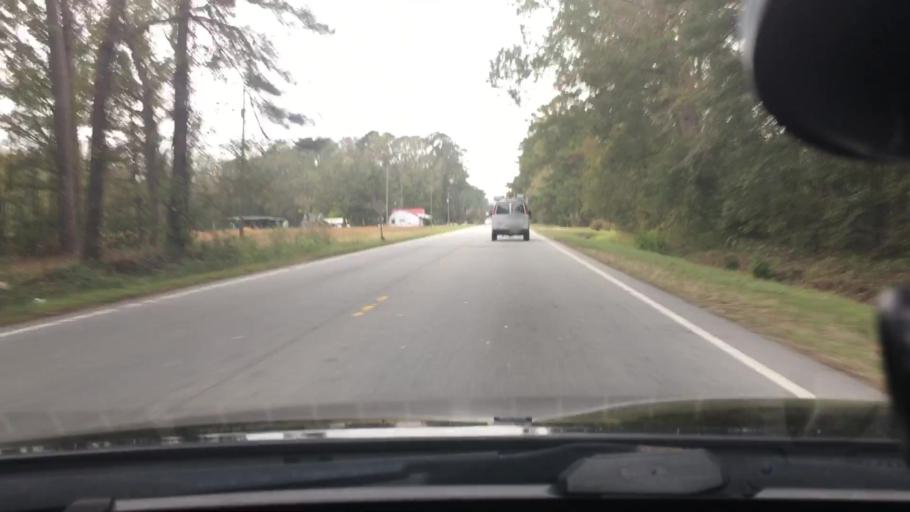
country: US
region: North Carolina
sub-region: Craven County
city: Vanceboro
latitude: 35.2636
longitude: -77.1041
